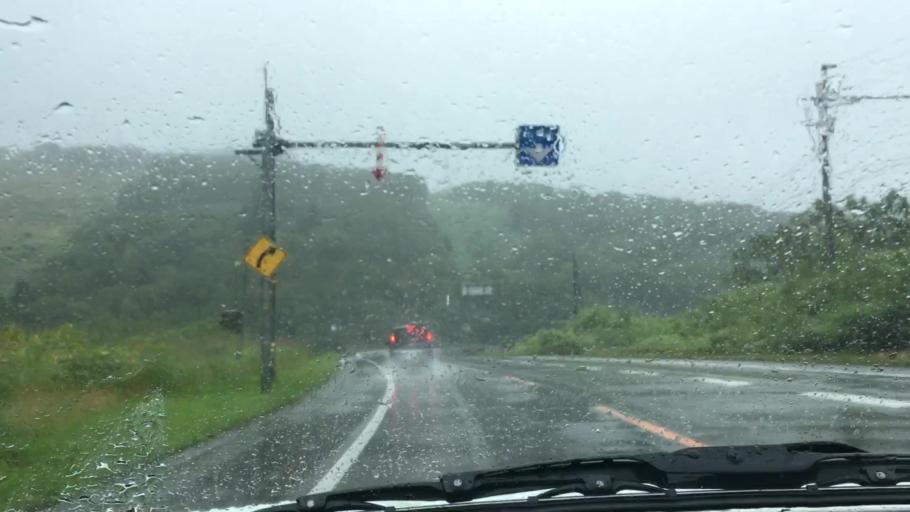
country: JP
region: Hokkaido
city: Sapporo
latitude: 42.8529
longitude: 141.0917
